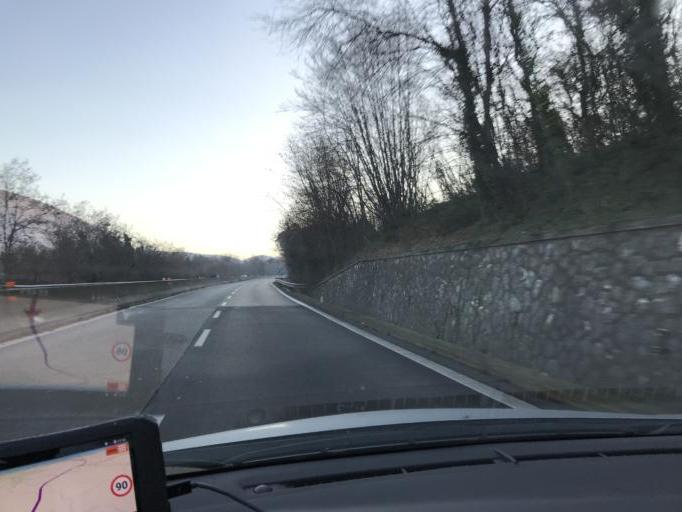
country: IT
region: Umbria
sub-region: Provincia di Terni
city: Terni
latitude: 42.5839
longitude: 12.6449
